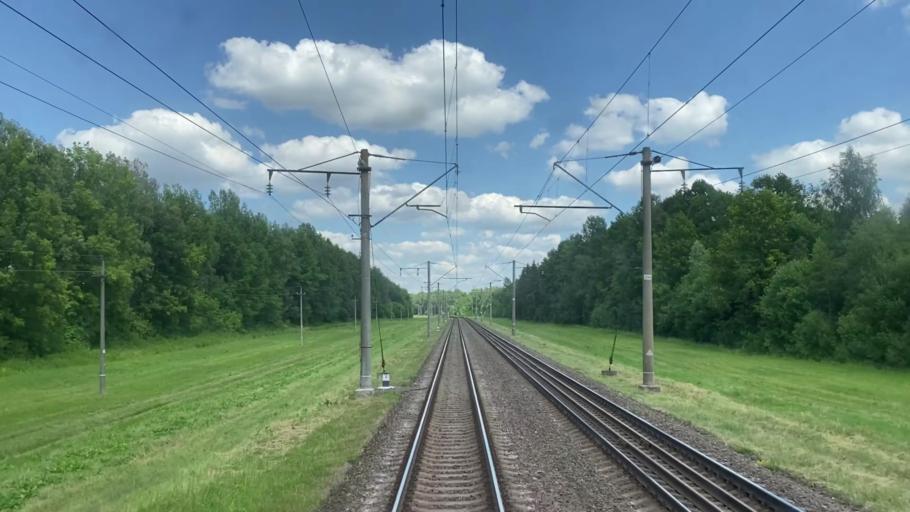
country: BY
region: Brest
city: Zhabinka
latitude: 52.2694
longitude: 24.1522
